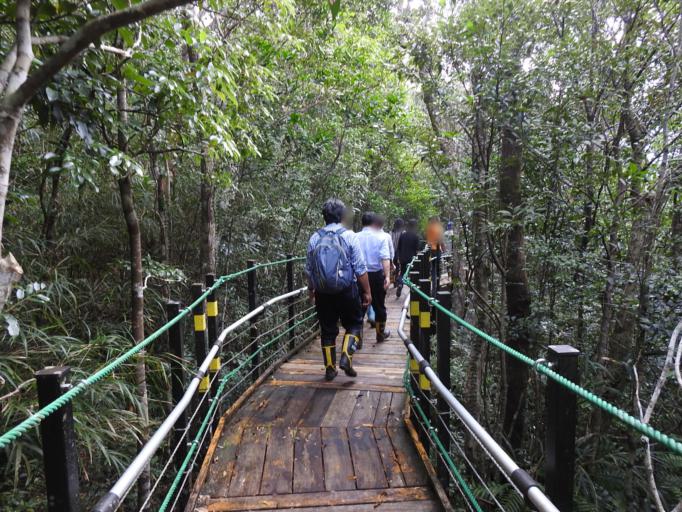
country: JP
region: Okinawa
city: Nago
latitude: 26.7208
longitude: 128.2660
